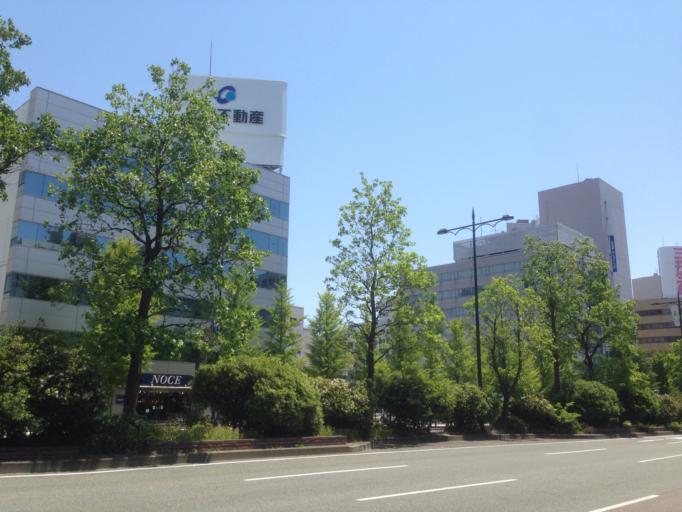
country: JP
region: Niigata
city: Niigata-shi
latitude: 37.9161
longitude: 139.0592
